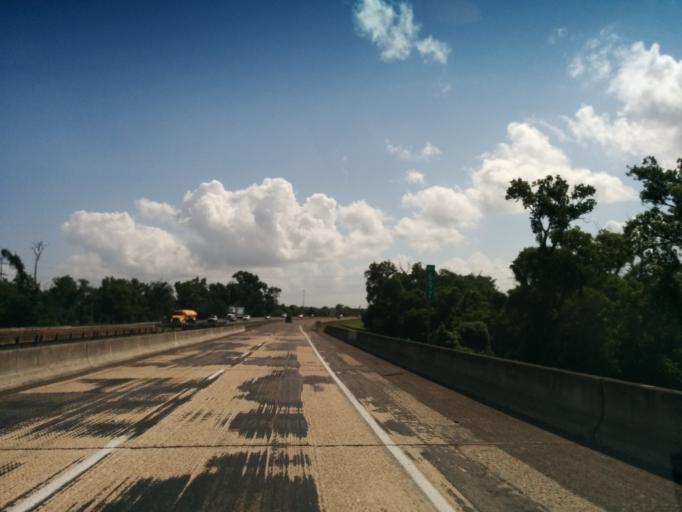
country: US
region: Texas
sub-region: Colorado County
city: Columbus
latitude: 29.6971
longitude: -96.5308
